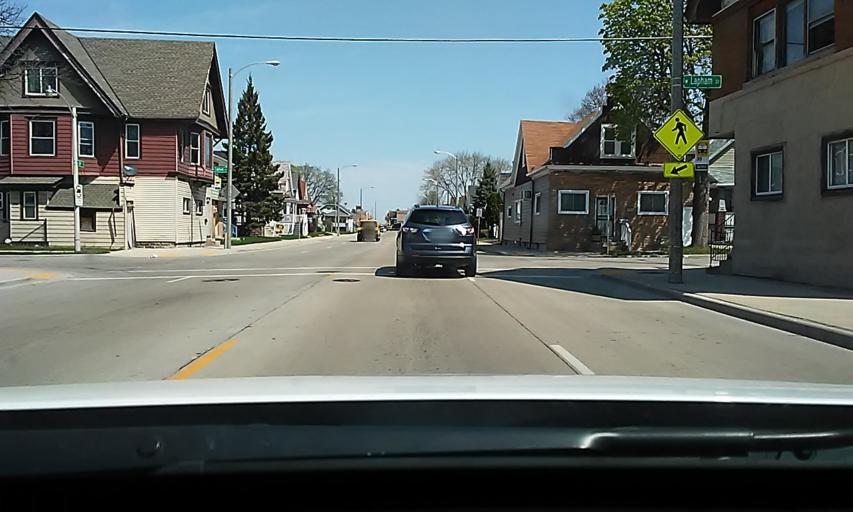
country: US
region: Wisconsin
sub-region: Milwaukee County
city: West Milwaukee
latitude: 43.0138
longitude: -87.9575
